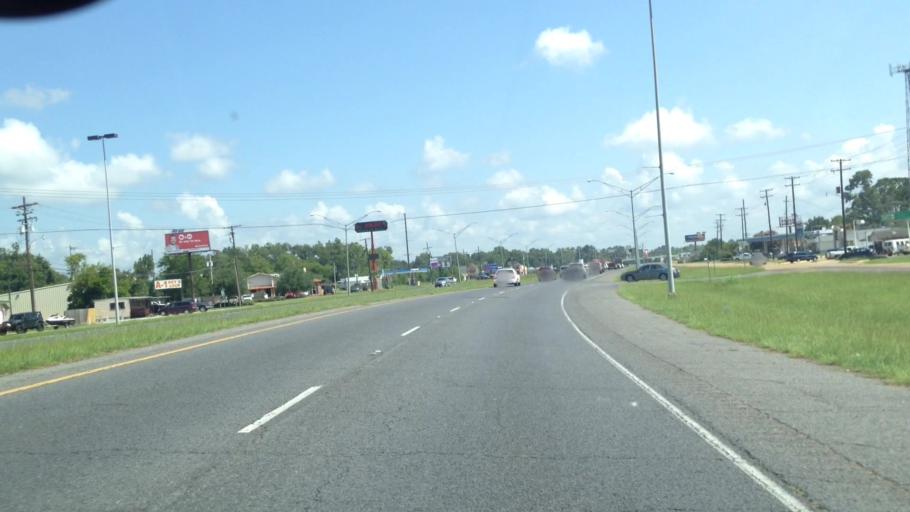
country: US
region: Louisiana
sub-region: Rapides Parish
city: Alexandria
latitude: 31.3018
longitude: -92.4800
